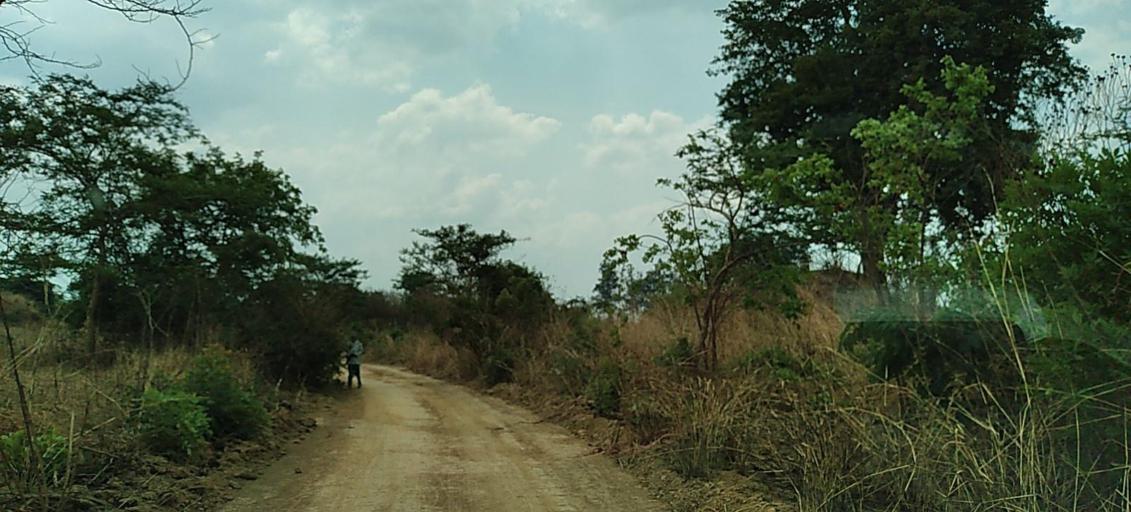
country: ZM
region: Copperbelt
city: Chililabombwe
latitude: -12.3528
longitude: 27.8015
